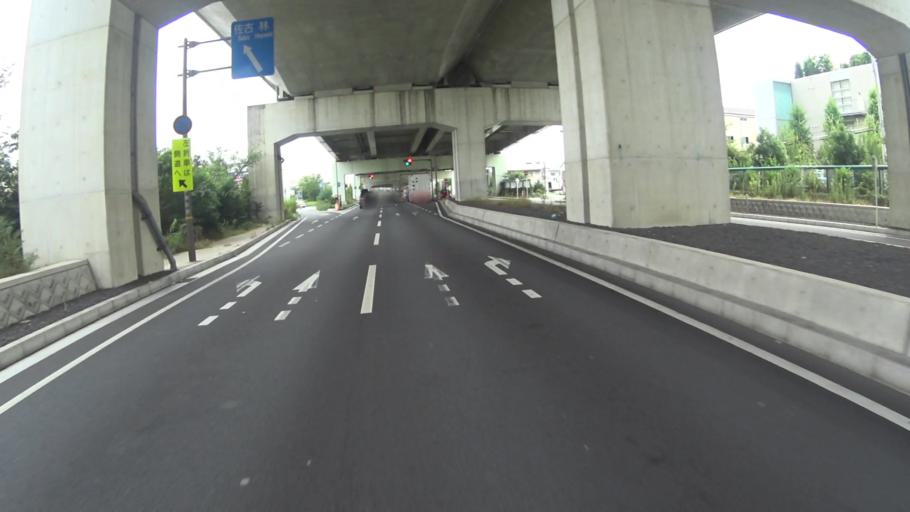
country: JP
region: Kyoto
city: Yawata
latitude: 34.8825
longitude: 135.7491
